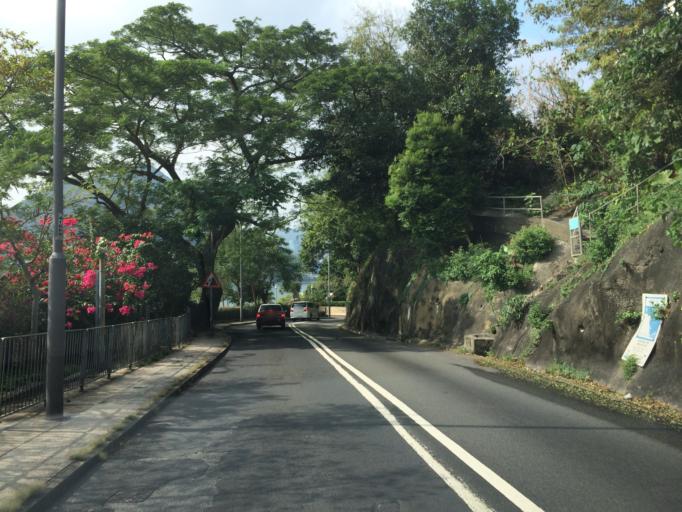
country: HK
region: Wanchai
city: Wan Chai
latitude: 22.2393
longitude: 114.1882
